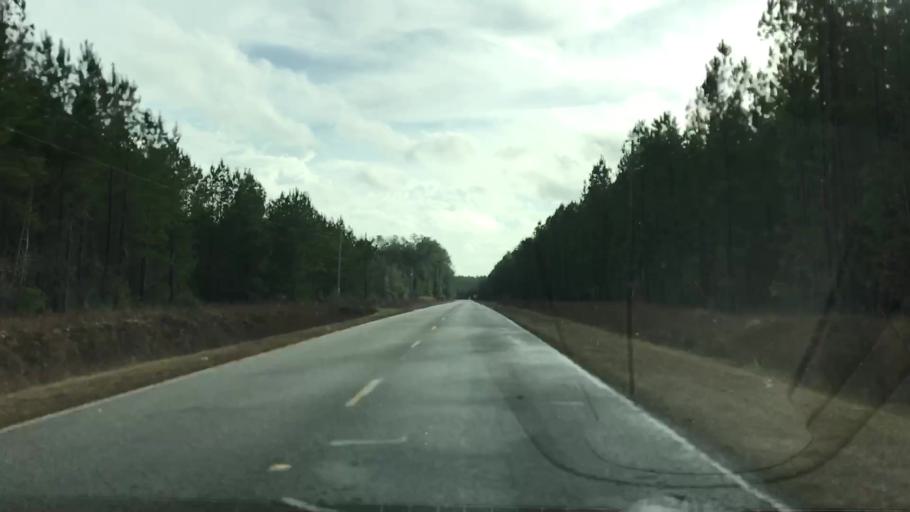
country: US
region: South Carolina
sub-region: Williamsburg County
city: Andrews
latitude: 33.4276
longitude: -79.5946
